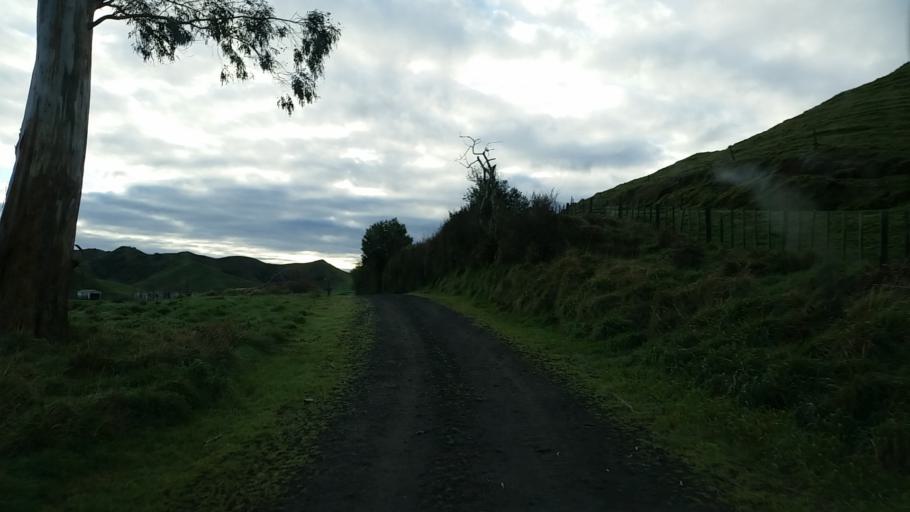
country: NZ
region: Taranaki
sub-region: South Taranaki District
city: Eltham
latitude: -39.3171
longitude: 174.3799
